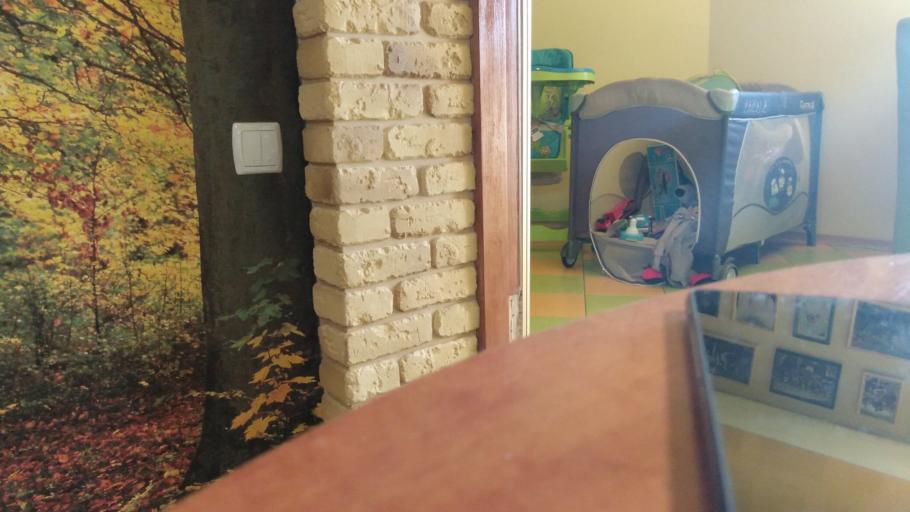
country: RU
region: Tverskaya
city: Bologoye
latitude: 57.9493
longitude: 34.1670
